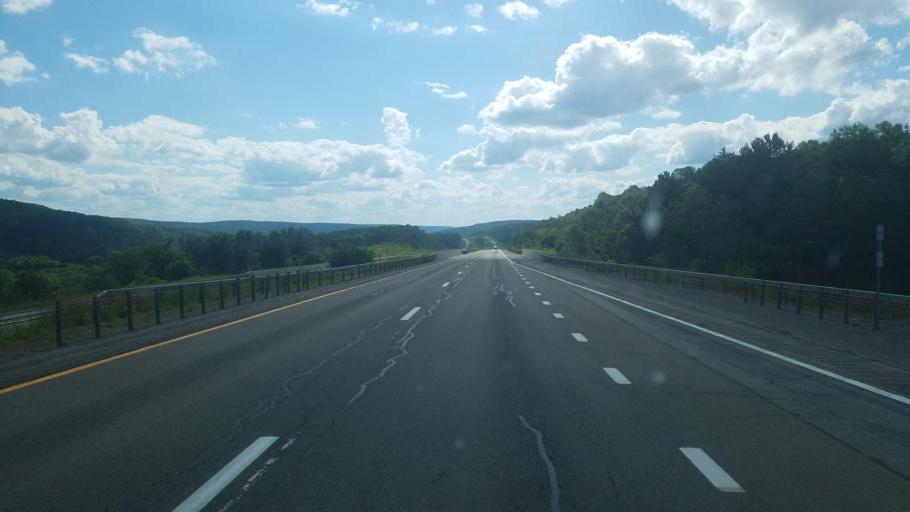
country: US
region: New York
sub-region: Allegany County
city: Alfred
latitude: 42.3055
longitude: -77.8771
